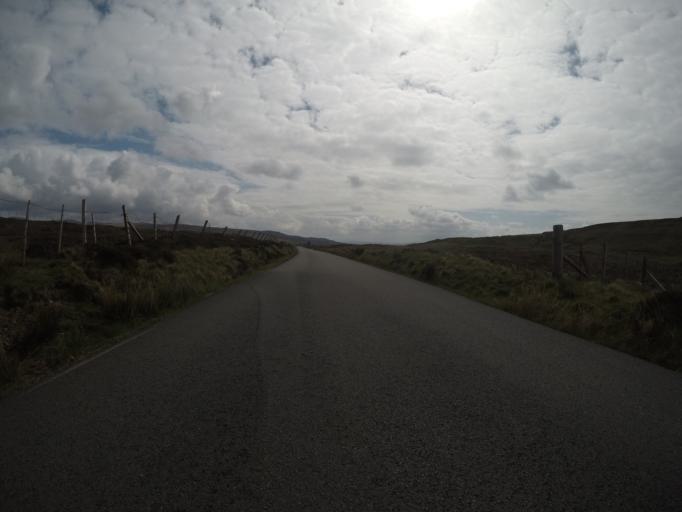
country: GB
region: Scotland
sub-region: Highland
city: Portree
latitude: 57.5973
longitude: -6.3756
